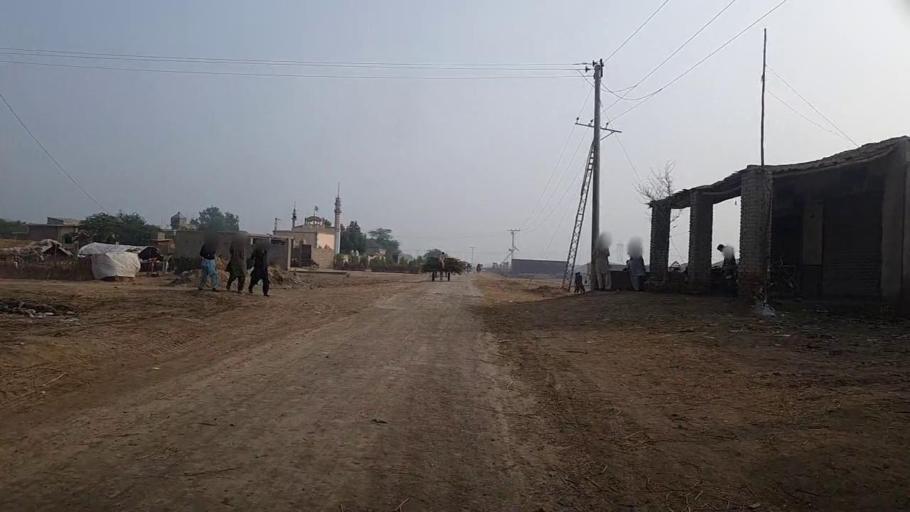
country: PK
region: Sindh
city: Phulji
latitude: 26.8251
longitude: 67.7540
